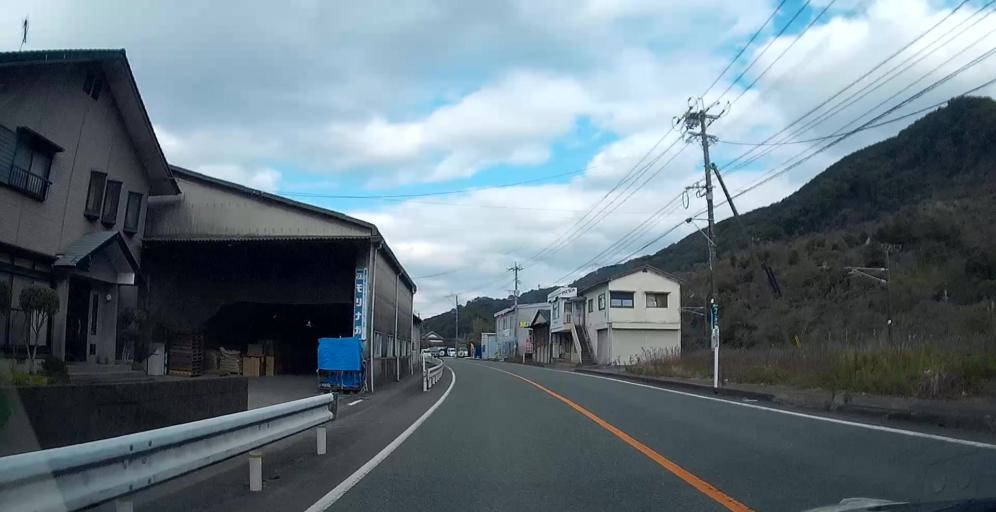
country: JP
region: Kumamoto
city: Yatsushiro
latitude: 32.4563
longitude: 130.5990
